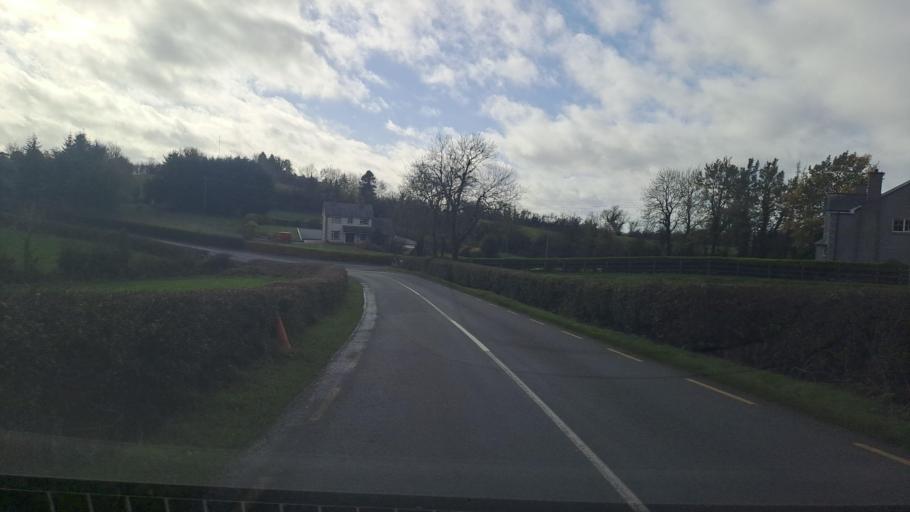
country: IE
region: Ulster
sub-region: County Monaghan
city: Monaghan
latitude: 54.1589
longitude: -7.0044
